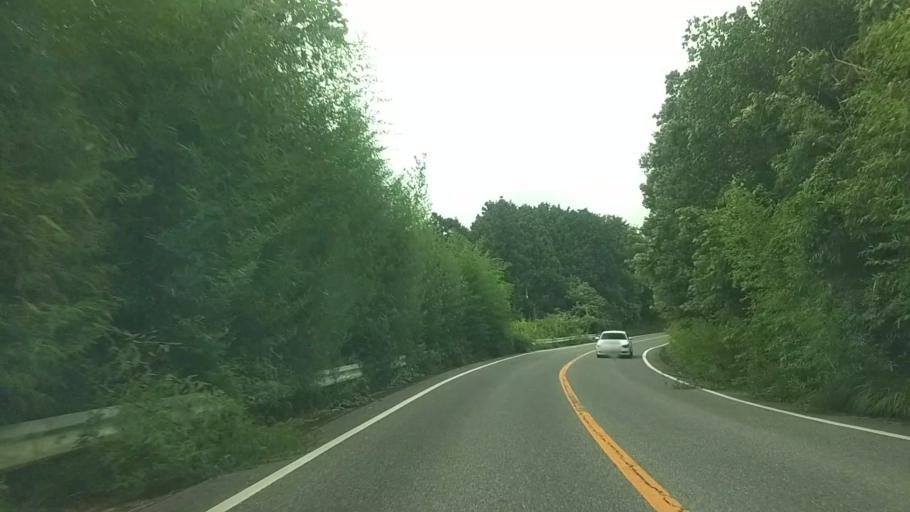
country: JP
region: Chiba
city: Kimitsu
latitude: 35.2393
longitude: 140.0066
